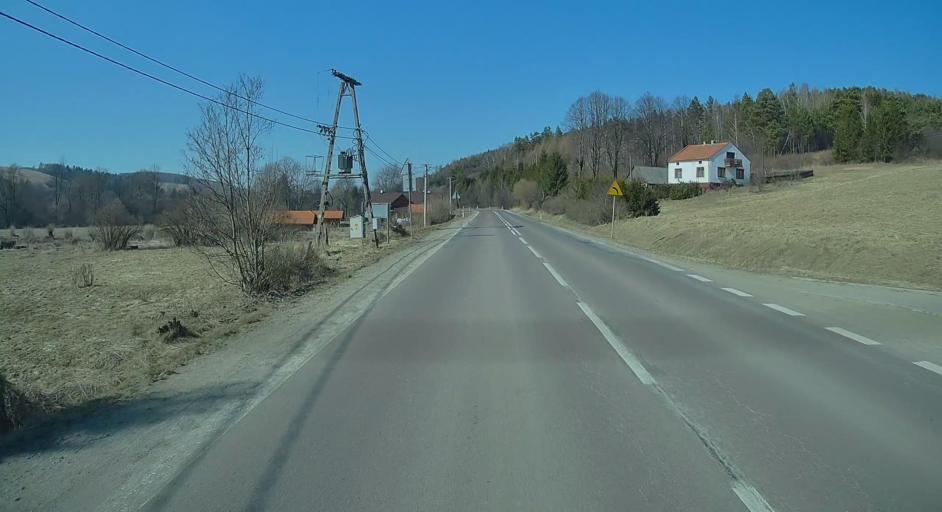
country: PL
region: Subcarpathian Voivodeship
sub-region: Powiat przemyski
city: Bircza
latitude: 49.5734
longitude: 22.5518
